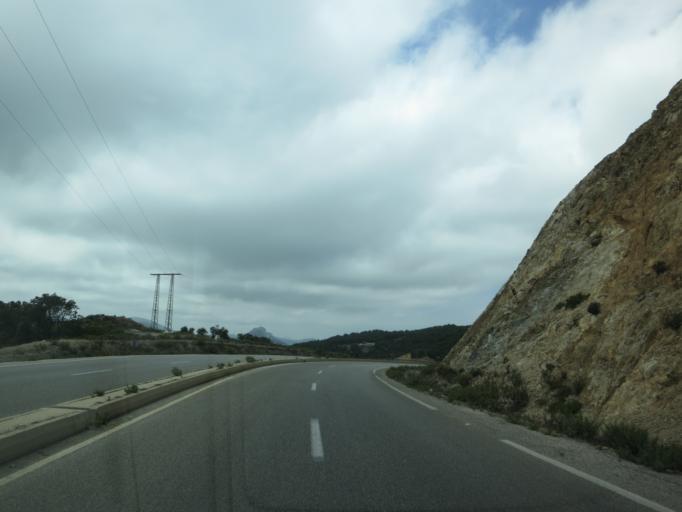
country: ES
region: Ceuta
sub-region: Ceuta
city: Ceuta
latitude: 35.8765
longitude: -5.3985
